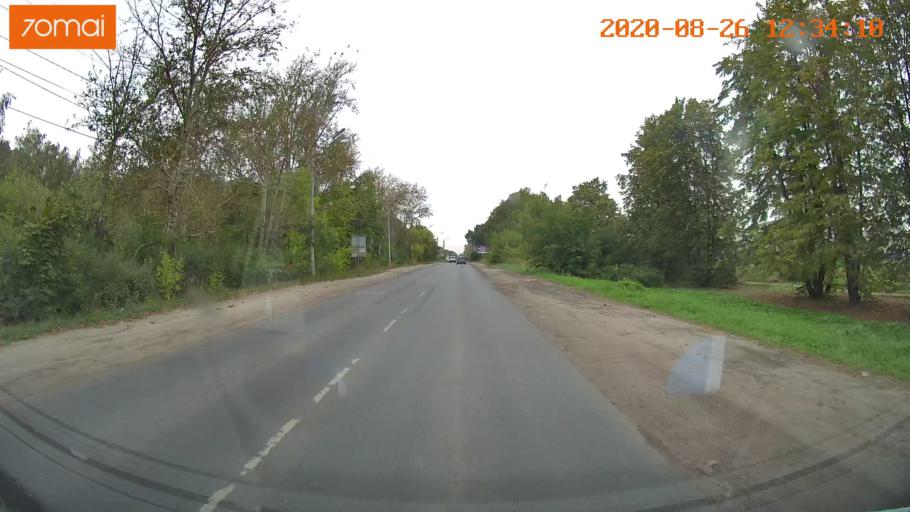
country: RU
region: Rjazan
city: Ryazan'
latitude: 54.5862
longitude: 39.7722
